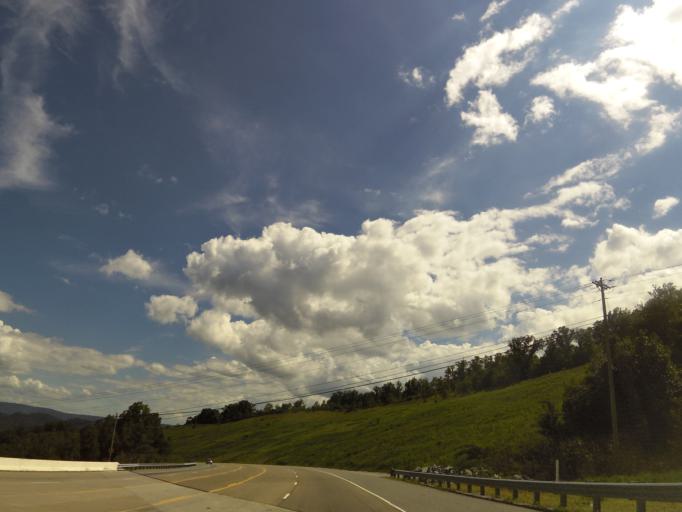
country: US
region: Tennessee
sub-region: Claiborne County
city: Tazewell
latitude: 36.4296
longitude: -83.5577
